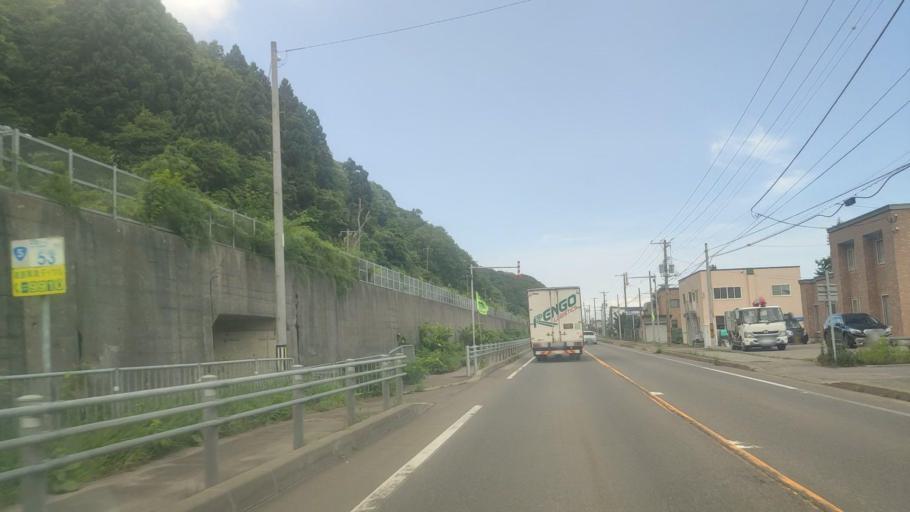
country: JP
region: Hokkaido
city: Nanae
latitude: 42.1580
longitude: 140.4745
